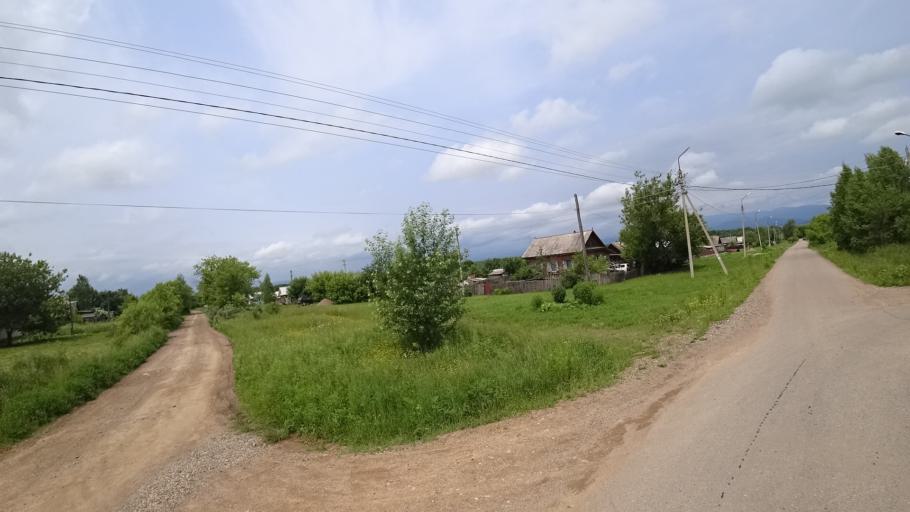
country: RU
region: Primorskiy
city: Novosysoyevka
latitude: 44.2352
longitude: 133.3591
